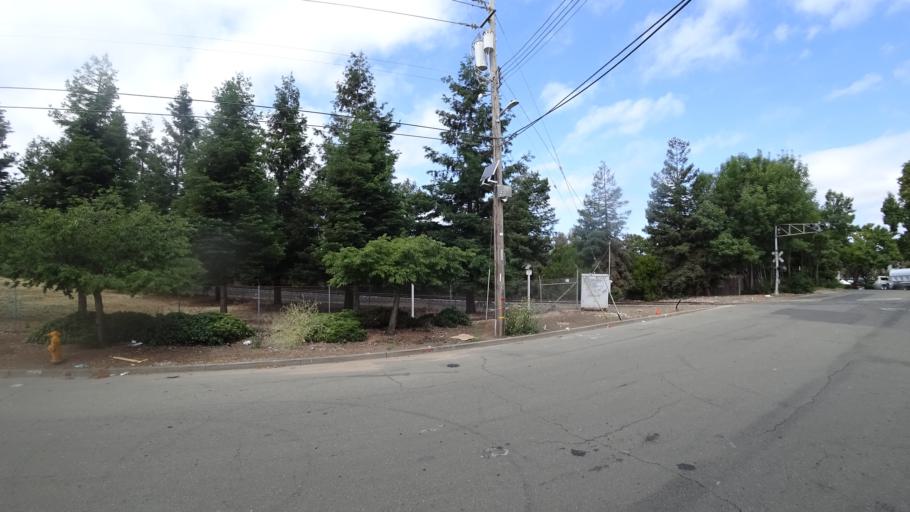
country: US
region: California
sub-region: Alameda County
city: Union City
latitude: 37.6144
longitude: -122.0470
